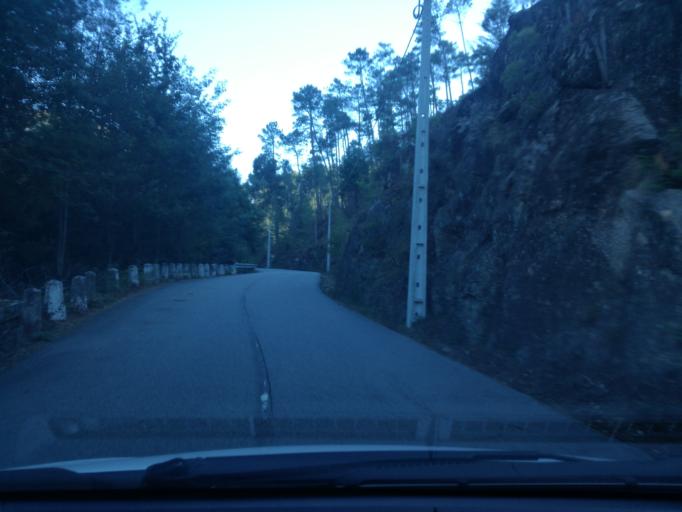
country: PT
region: Braga
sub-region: Vieira do Minho
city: Real
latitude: 41.7415
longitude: -8.1555
